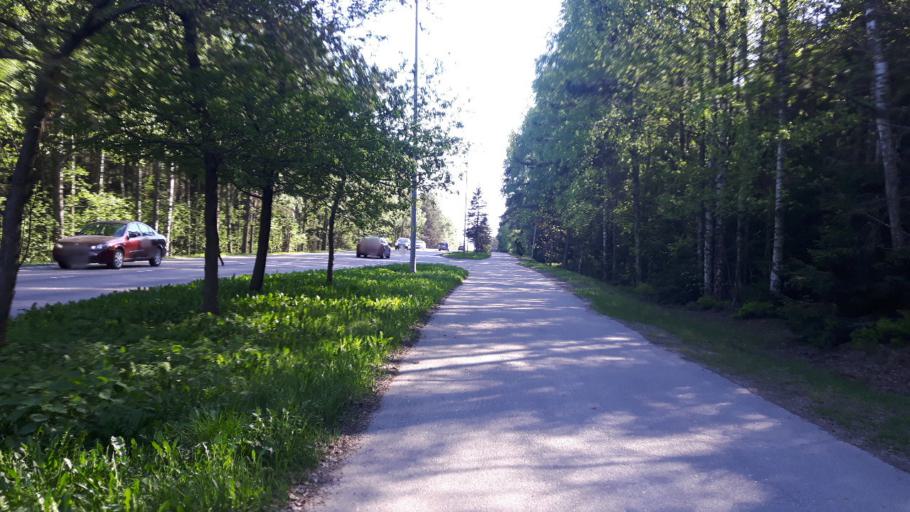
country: FI
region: Kymenlaakso
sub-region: Kotka-Hamina
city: Kotka
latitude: 60.4484
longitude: 26.8944
